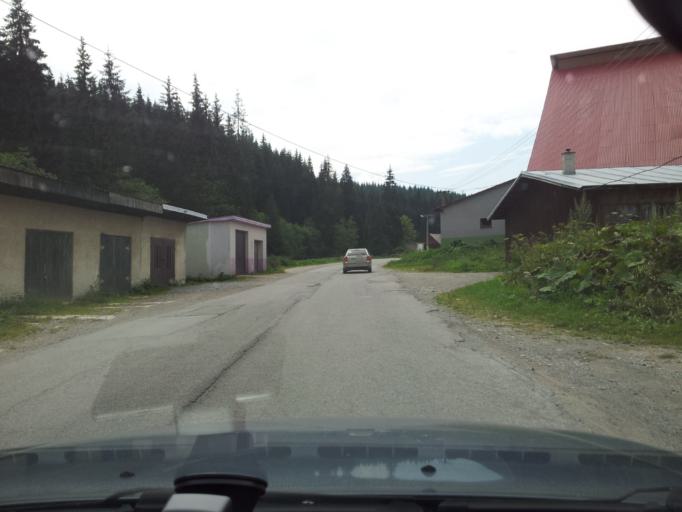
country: SK
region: Zilinsky
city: Oravska Lesna
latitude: 49.3652
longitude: 19.1824
